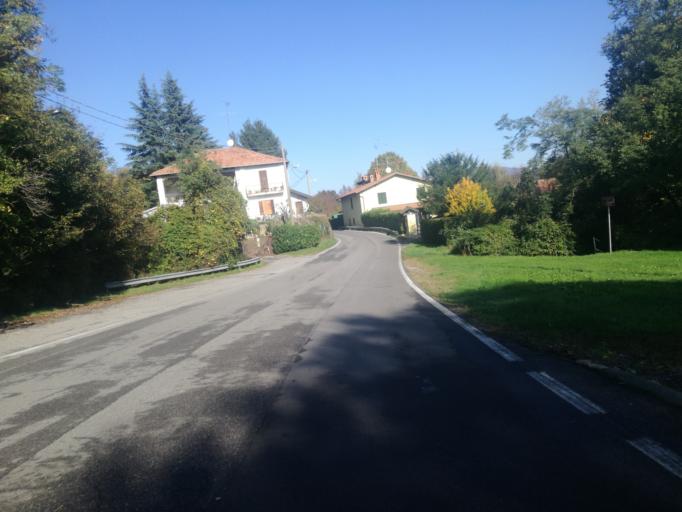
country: IT
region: Lombardy
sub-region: Citta metropolitana di Milano
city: Trezzo sull'Adda
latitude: 45.6163
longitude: 9.5129
